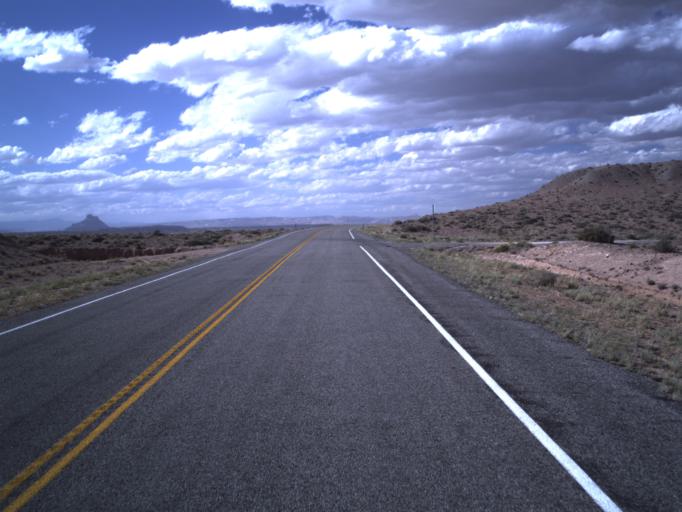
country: US
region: Utah
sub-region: Emery County
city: Ferron
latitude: 38.3372
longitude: -110.6873
